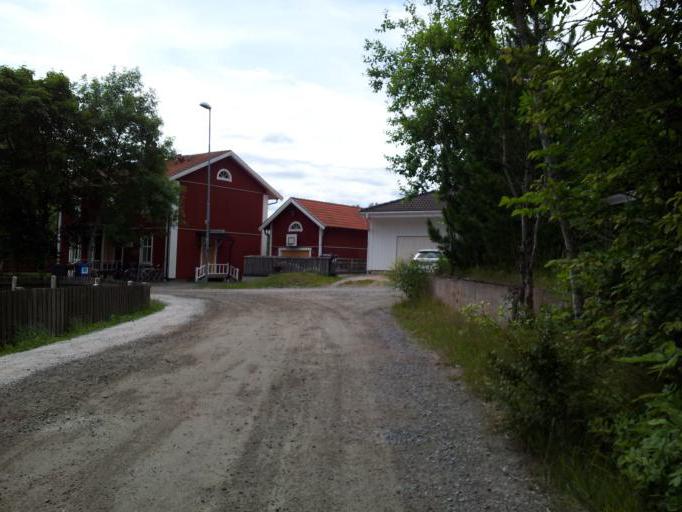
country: SE
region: Uppsala
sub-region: Uppsala Kommun
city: Saevja
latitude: 59.7875
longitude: 17.6600
